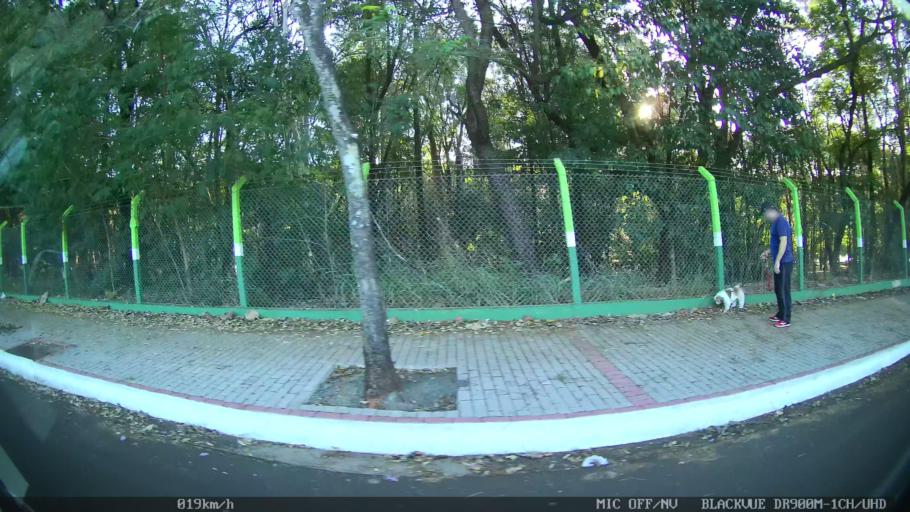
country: BR
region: Sao Paulo
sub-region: Nova Odessa
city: Nova Odessa
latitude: -22.7855
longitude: -47.2929
